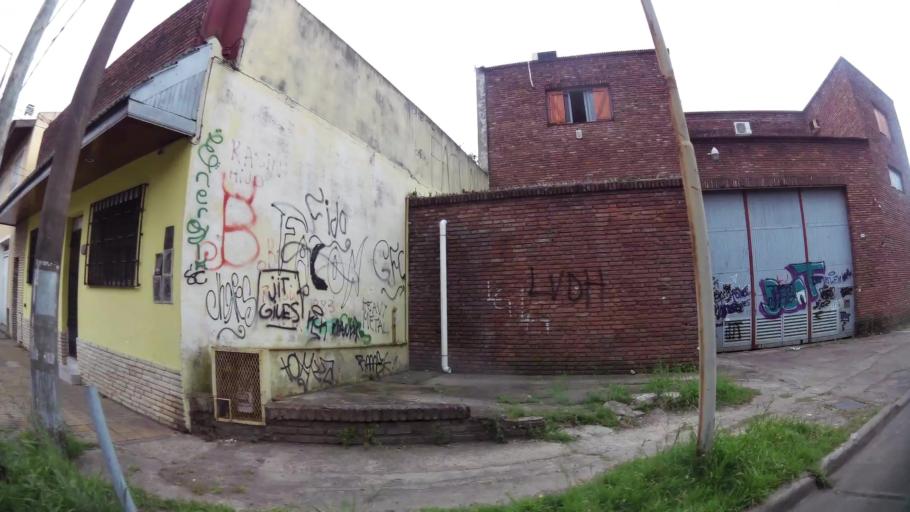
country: AR
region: Buenos Aires
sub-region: Partido de Avellaneda
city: Avellaneda
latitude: -34.6718
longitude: -58.3491
